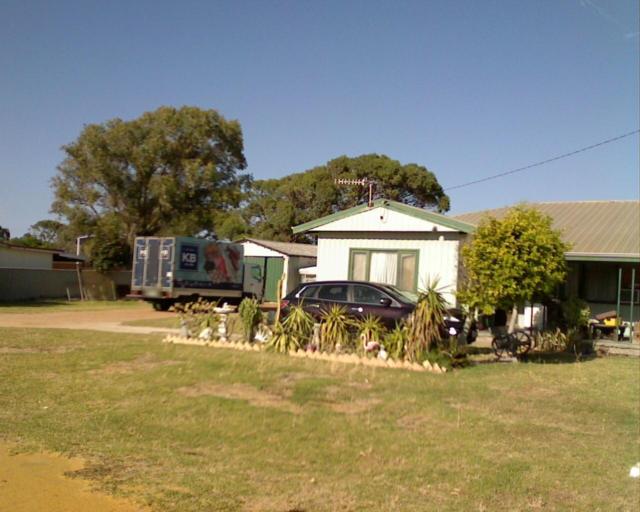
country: AU
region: Western Australia
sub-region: Dandaragan
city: Jurien Bay
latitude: -30.0627
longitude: 114.9688
